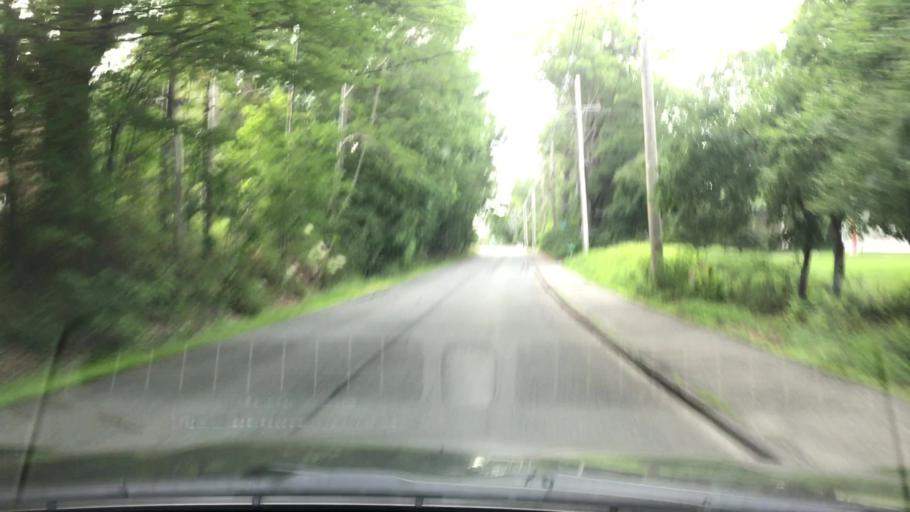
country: US
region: Maine
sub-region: Hancock County
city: Bar Harbor
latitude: 44.3701
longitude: -68.1962
